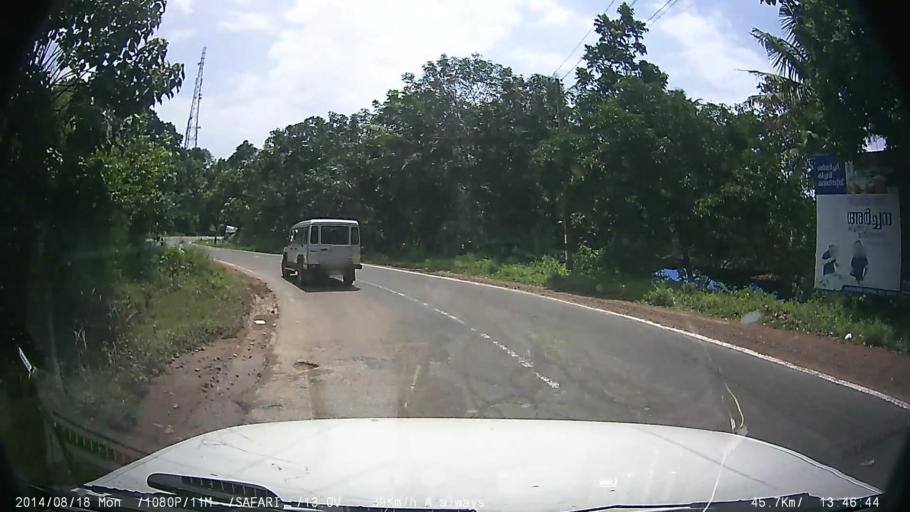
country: IN
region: Kerala
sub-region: Kottayam
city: Palackattumala
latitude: 9.6983
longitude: 76.5583
